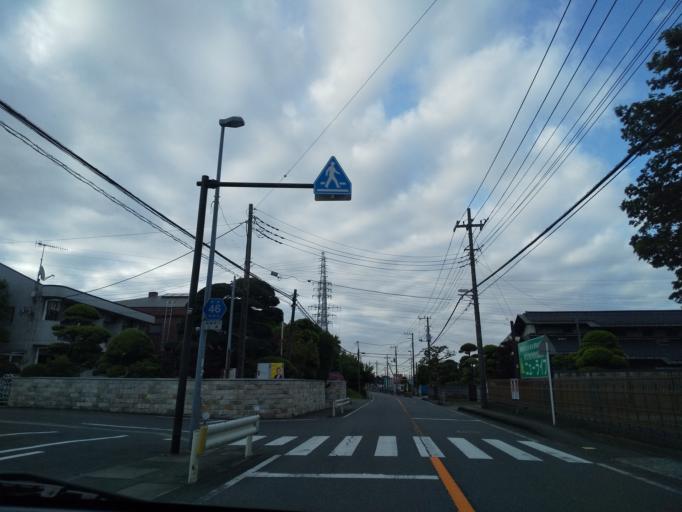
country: JP
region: Kanagawa
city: Zama
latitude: 35.5373
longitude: 139.3690
